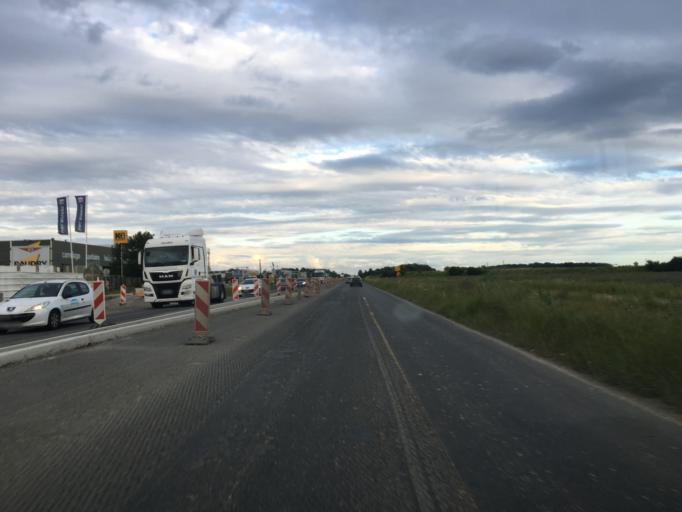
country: FR
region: Ile-de-France
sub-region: Departement de Seine-et-Marne
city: Servon
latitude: 48.7083
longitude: 2.5869
